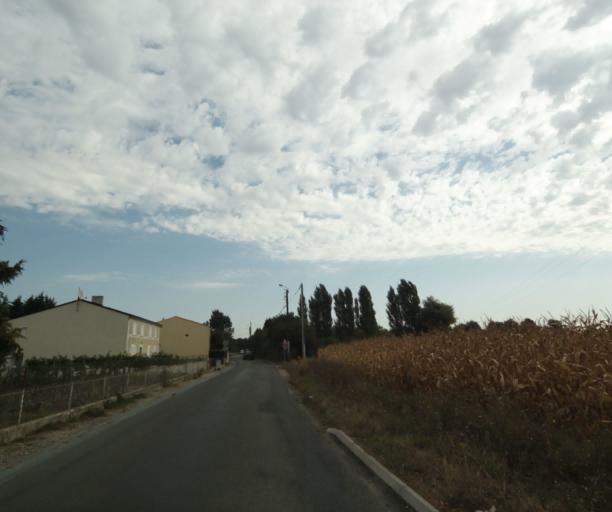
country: FR
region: Poitou-Charentes
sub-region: Departement de la Charente-Maritime
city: Tonnay-Charente
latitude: 45.9575
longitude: -0.8774
